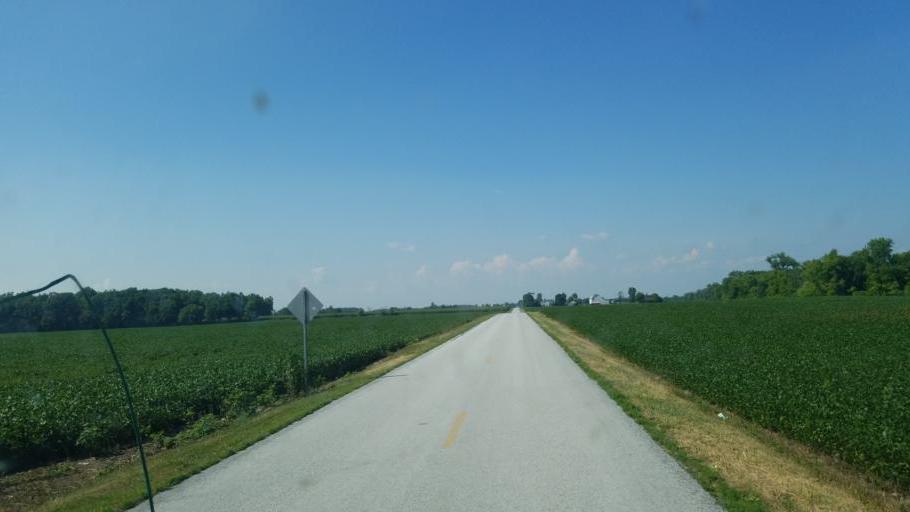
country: US
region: Ohio
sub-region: Hardin County
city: Forest
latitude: 40.6895
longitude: -83.4957
